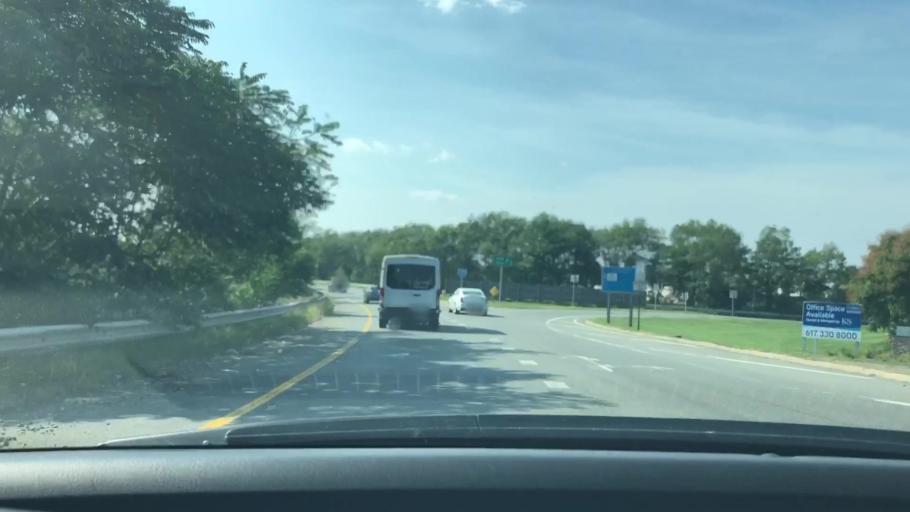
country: US
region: Massachusetts
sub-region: Norfolk County
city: Dedham
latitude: 42.2236
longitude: -71.1701
